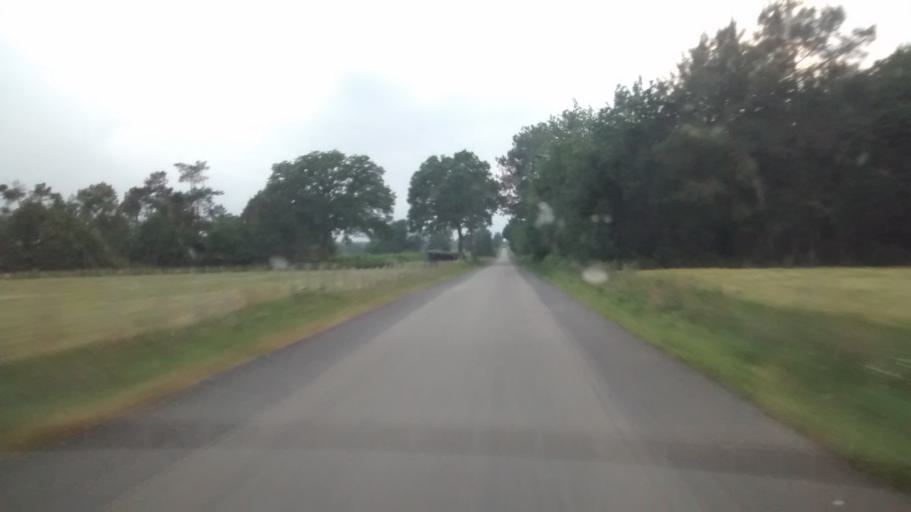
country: FR
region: Brittany
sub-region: Departement du Morbihan
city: Saint-Martin-sur-Oust
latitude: 47.7302
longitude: -2.2952
